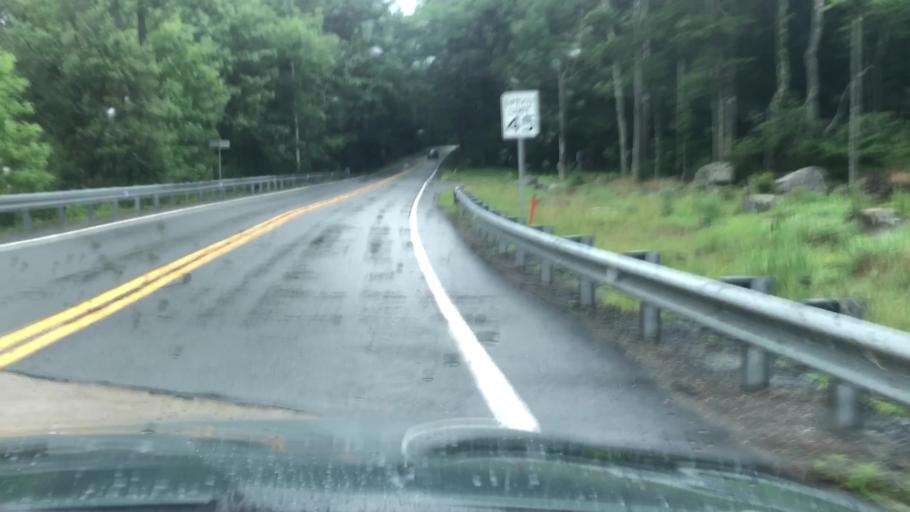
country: US
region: Pennsylvania
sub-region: Monroe County
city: Mountainhome
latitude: 41.2527
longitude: -75.2358
